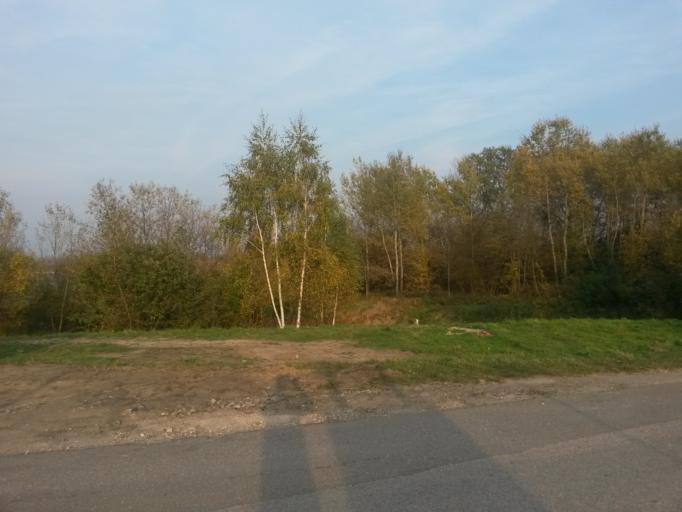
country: PL
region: Masovian Voivodeship
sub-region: Powiat piaseczynski
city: Konstancin-Jeziorna
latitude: 52.1211
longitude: 21.1740
